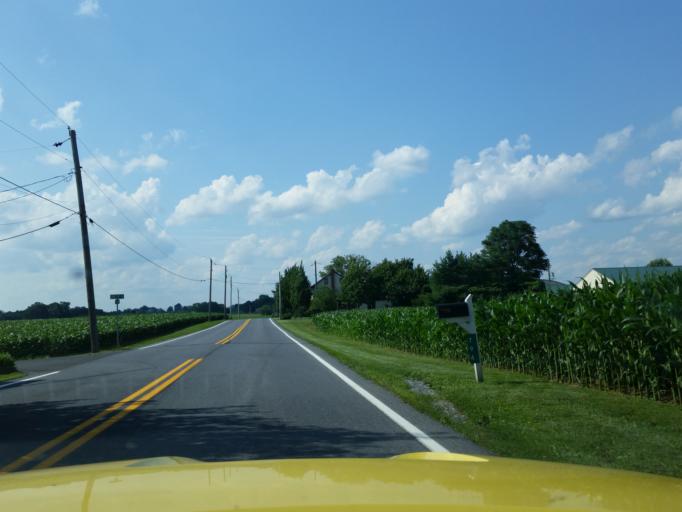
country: US
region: Pennsylvania
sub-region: Lancaster County
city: Manheim
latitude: 40.1518
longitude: -76.4425
